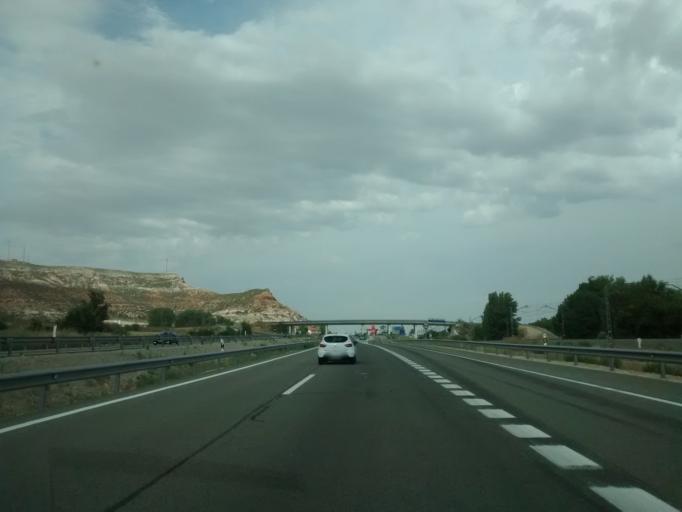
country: ES
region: Castille and Leon
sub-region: Provincia de Soria
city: Arcos de Jalon
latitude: 41.2215
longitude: -2.2652
